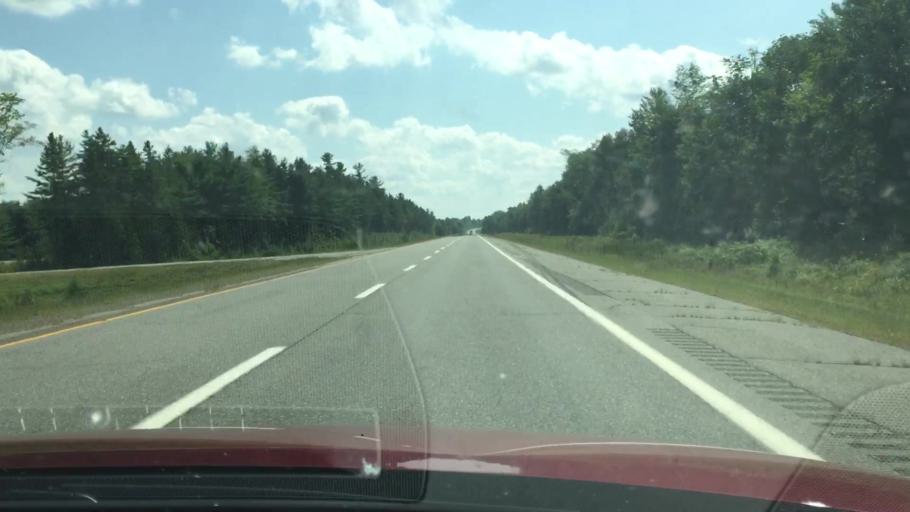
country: US
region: Maine
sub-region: Penobscot County
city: Lincoln
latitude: 45.4436
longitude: -68.5910
